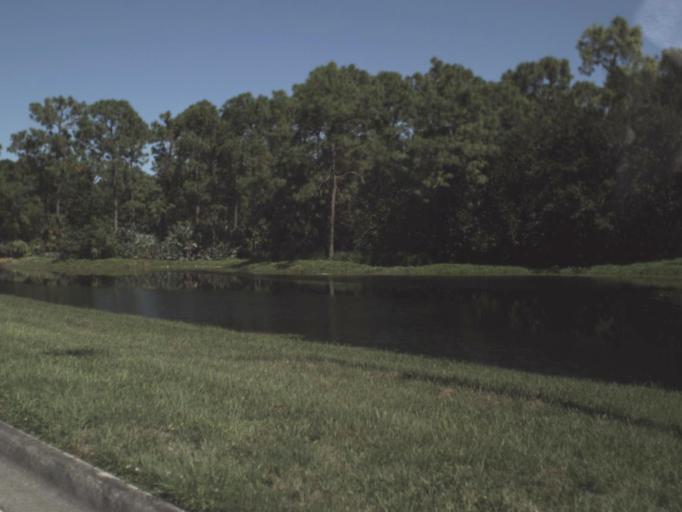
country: US
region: Florida
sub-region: Collier County
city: Pine Ridge
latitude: 26.1910
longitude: -81.7677
